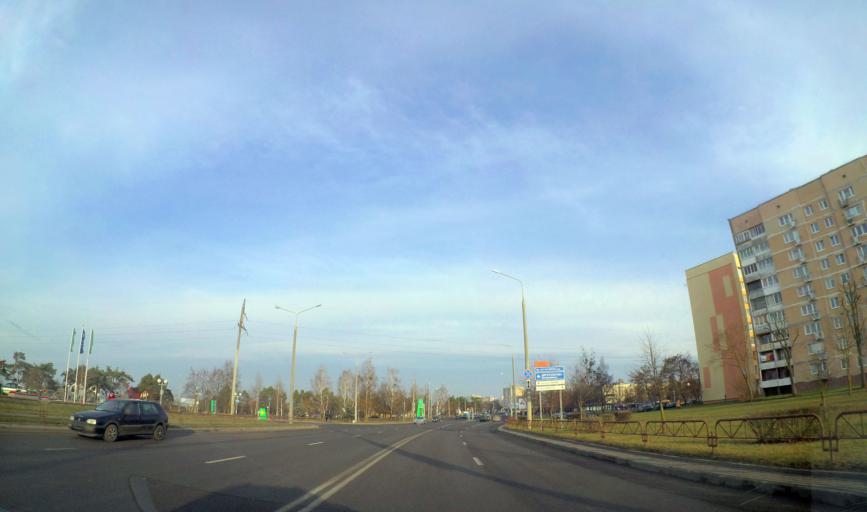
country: BY
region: Grodnenskaya
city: Hrodna
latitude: 53.6648
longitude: 23.7848
